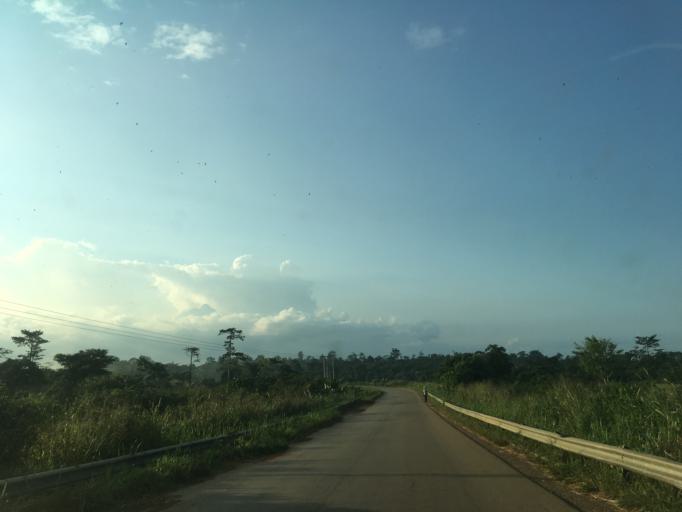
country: GH
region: Western
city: Bibiani
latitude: 6.5716
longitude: -2.3720
